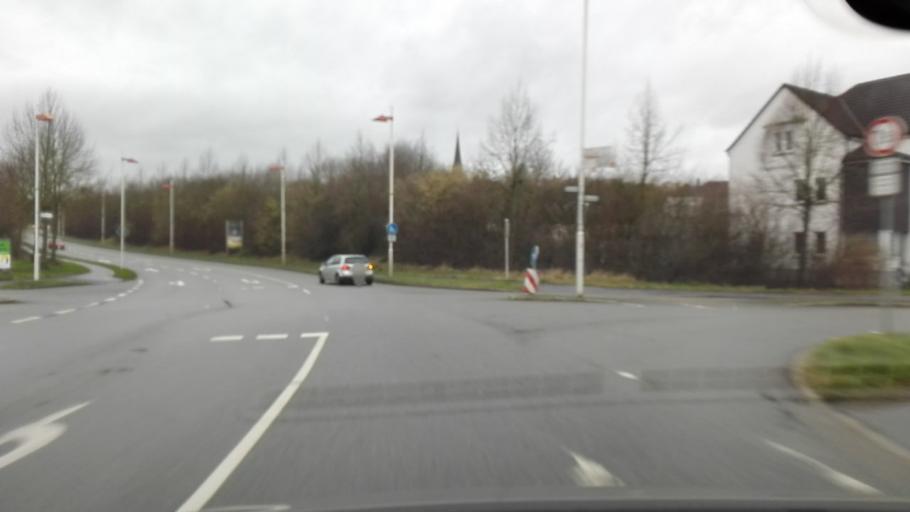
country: DE
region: North Rhine-Westphalia
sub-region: Regierungsbezirk Arnsberg
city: Frondenberg
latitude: 51.4701
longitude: 7.7681
